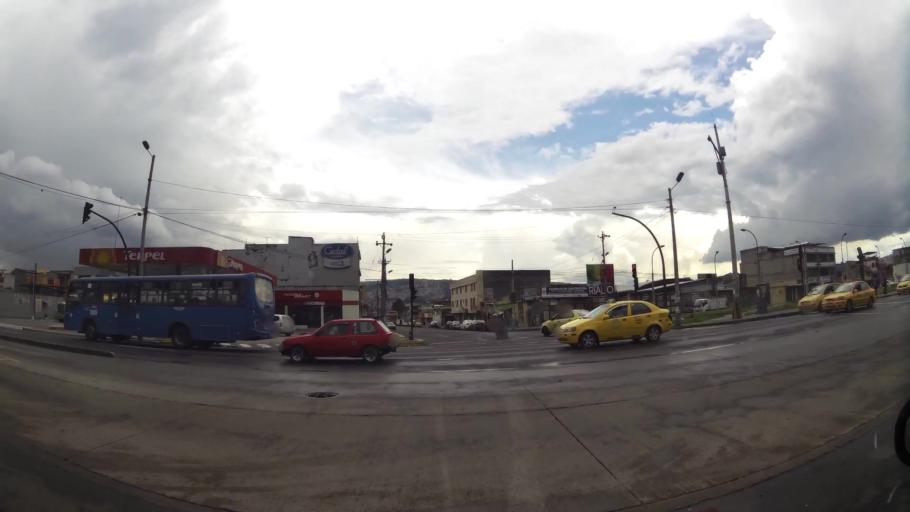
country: EC
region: Pichincha
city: Quito
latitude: -0.2621
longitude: -78.5481
